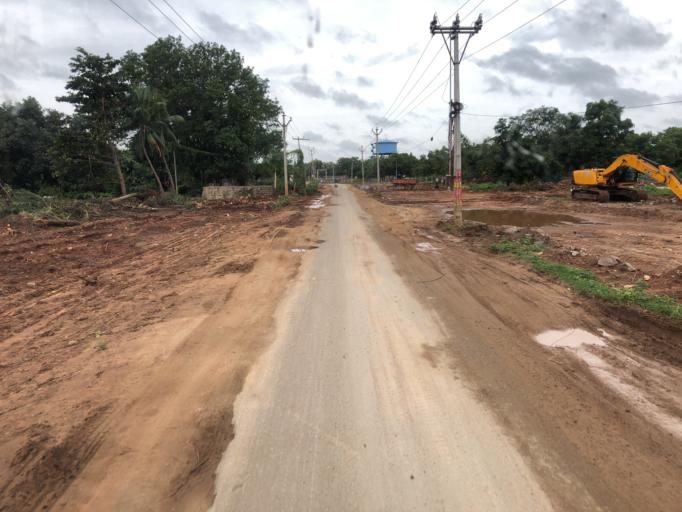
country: IN
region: Telangana
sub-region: Medak
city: Serilingampalle
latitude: 17.4301
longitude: 78.2977
